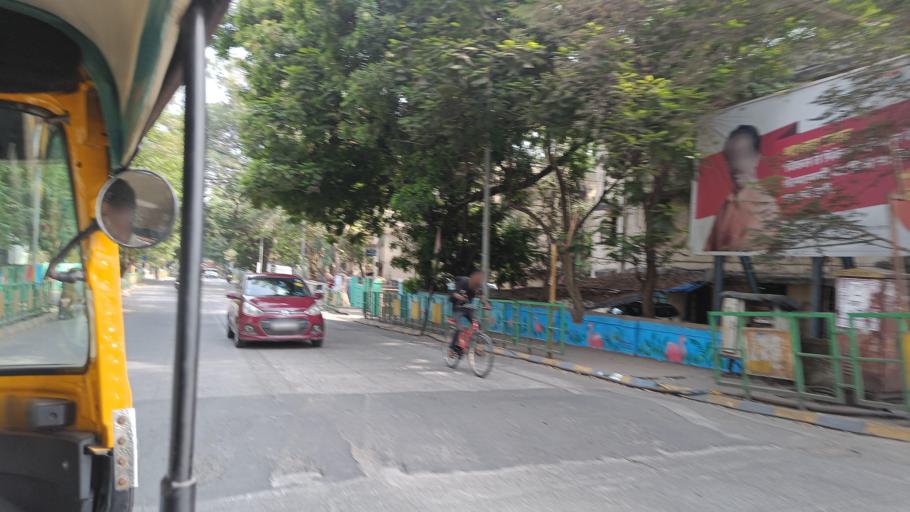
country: IN
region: Maharashtra
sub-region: Thane
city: Thane
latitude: 19.1811
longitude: 72.9678
